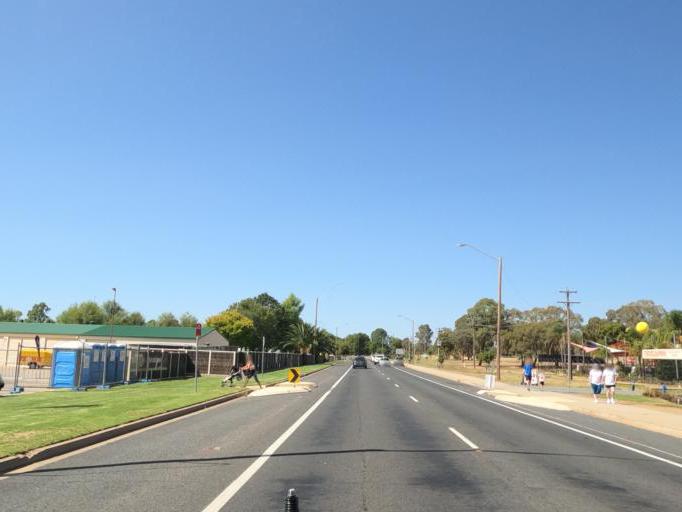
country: AU
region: New South Wales
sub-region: Corowa Shire
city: Mulwala
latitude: -35.9952
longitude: 146.0011
